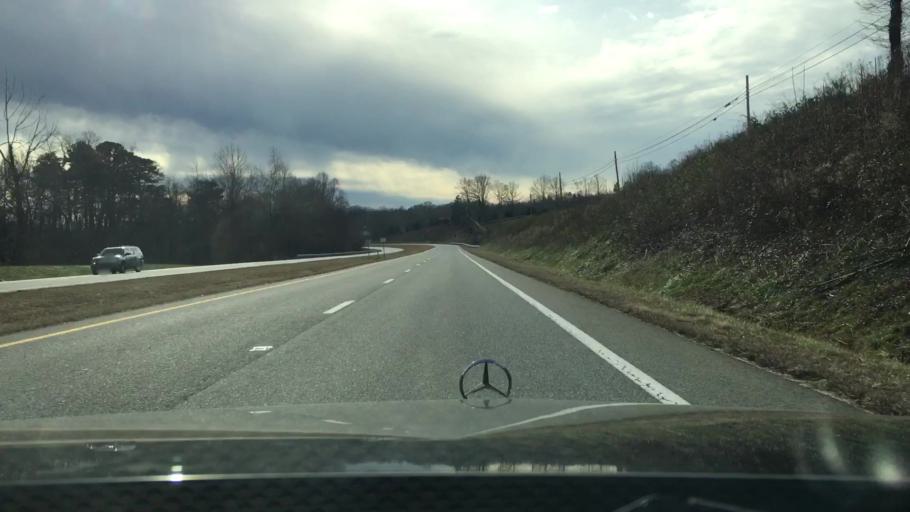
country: US
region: Virginia
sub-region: Pittsylvania County
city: Motley
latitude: 37.0599
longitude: -79.3481
